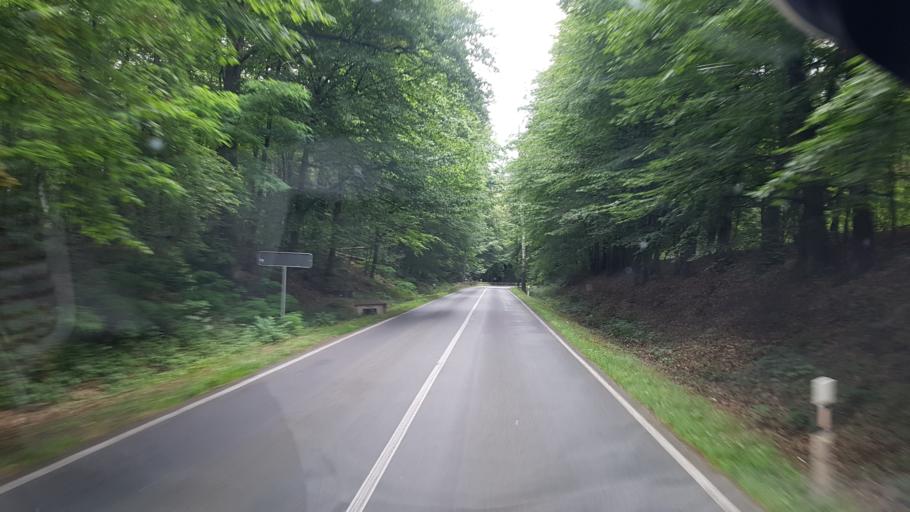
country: DE
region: Brandenburg
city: Lebusa
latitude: 51.7791
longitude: 13.3821
